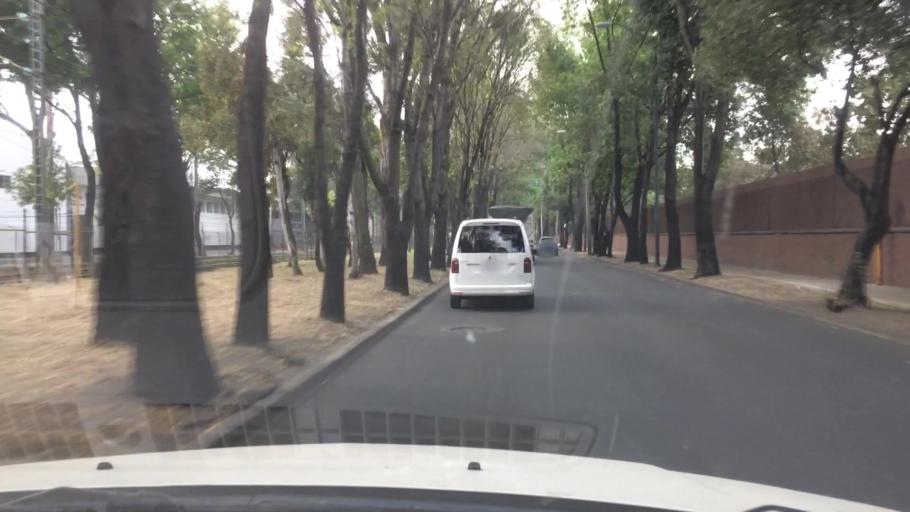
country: MX
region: Mexico City
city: Tlalpan
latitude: 19.2853
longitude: -99.1425
